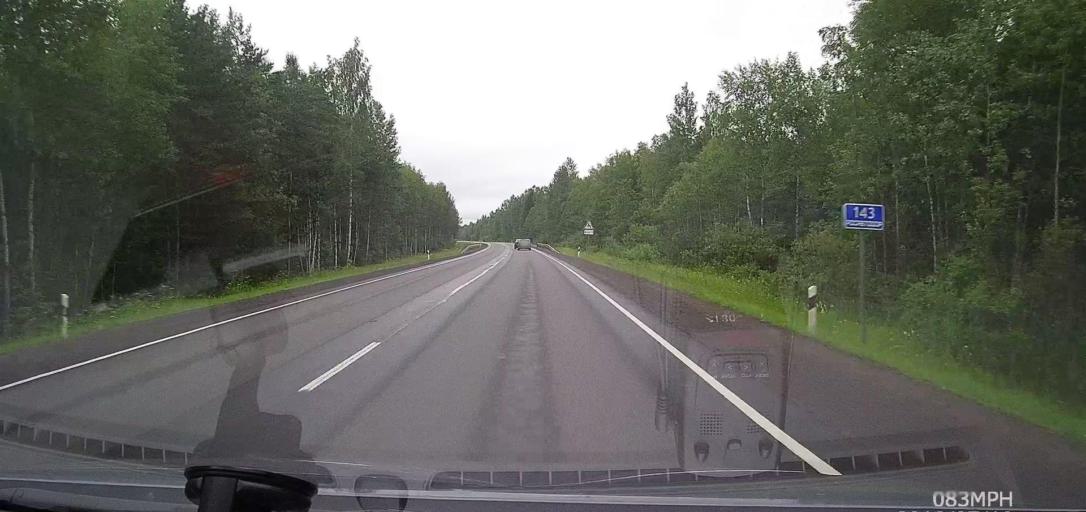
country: RU
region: Leningrad
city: Syas'stroy
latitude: 60.1862
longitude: 32.6400
